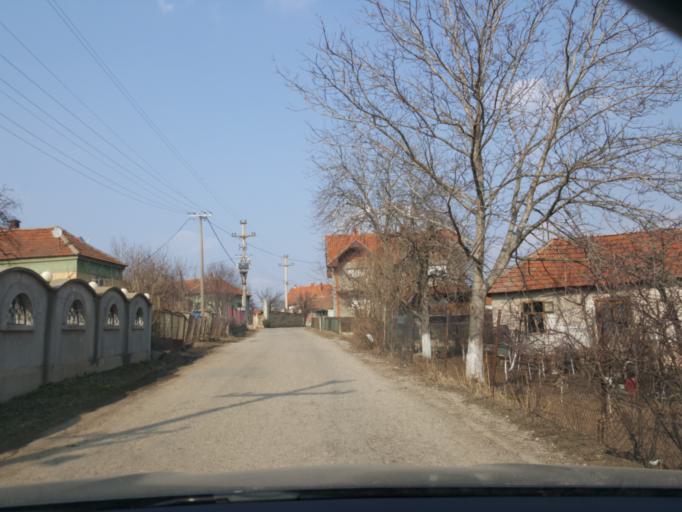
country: RS
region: Central Serbia
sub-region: Nisavski Okrug
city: Aleksinac
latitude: 43.5268
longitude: 21.7354
